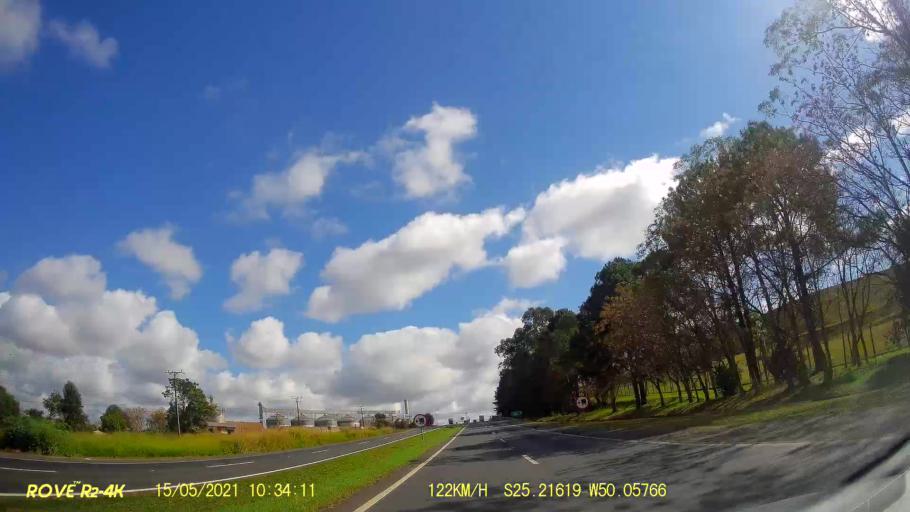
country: BR
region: Parana
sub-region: Ponta Grossa
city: Ponta Grossa
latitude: -25.2162
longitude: -50.0574
